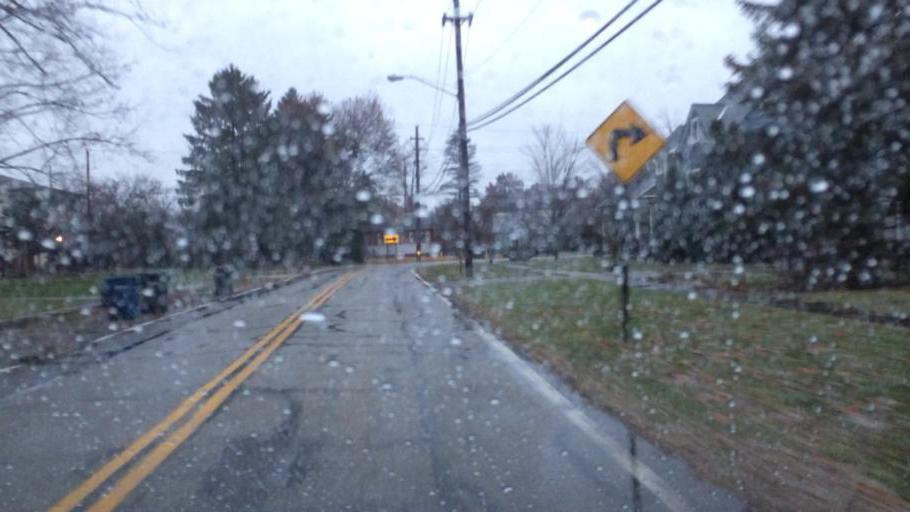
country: US
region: Ohio
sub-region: Cuyahoga County
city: Olmsted Falls
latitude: 41.3737
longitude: -81.9056
